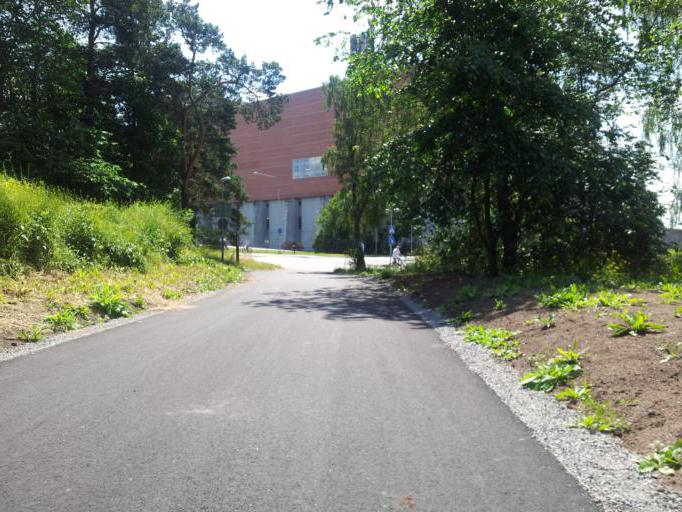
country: SE
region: Uppsala
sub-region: Uppsala Kommun
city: Uppsala
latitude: 59.8546
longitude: 17.6732
